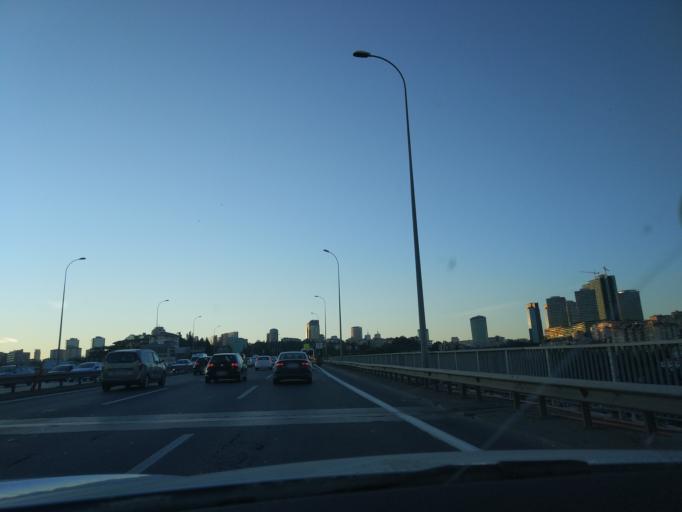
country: TR
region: Istanbul
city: UEskuedar
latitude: 41.0554
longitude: 29.0229
